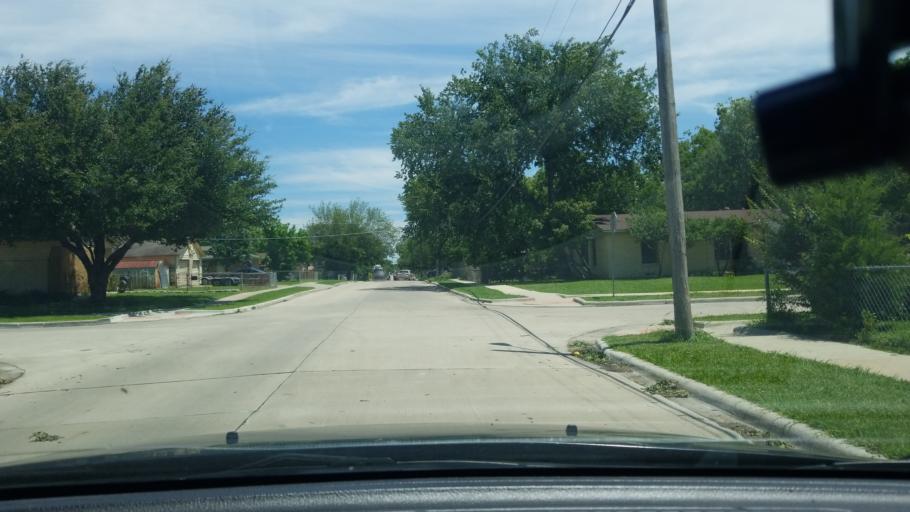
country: US
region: Texas
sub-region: Dallas County
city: Mesquite
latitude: 32.7880
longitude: -96.6132
